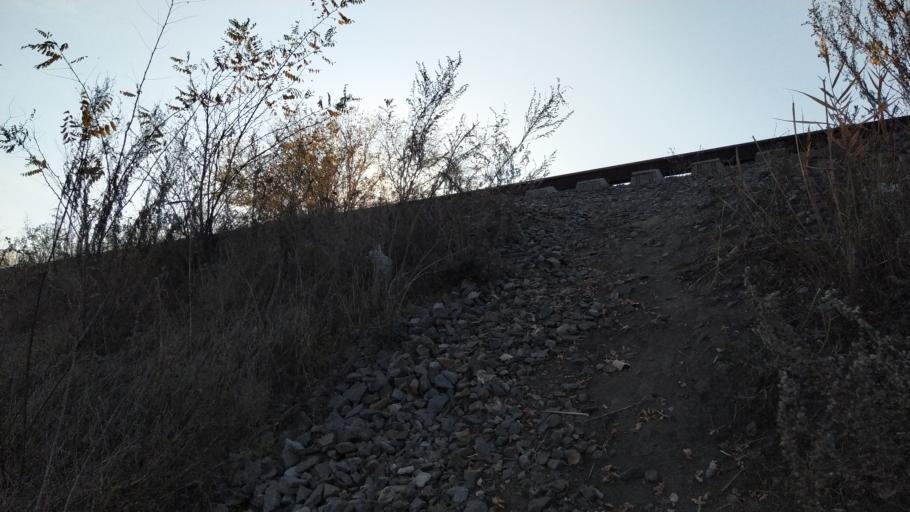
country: RU
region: Rostov
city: Bataysk
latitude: 47.1219
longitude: 39.7136
